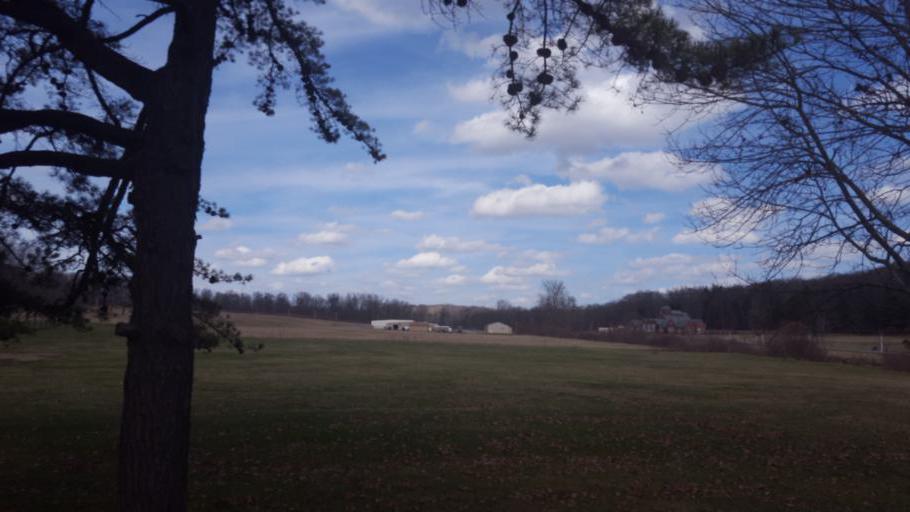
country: US
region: Ohio
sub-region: Knox County
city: Mount Vernon
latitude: 40.4144
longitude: -82.4541
